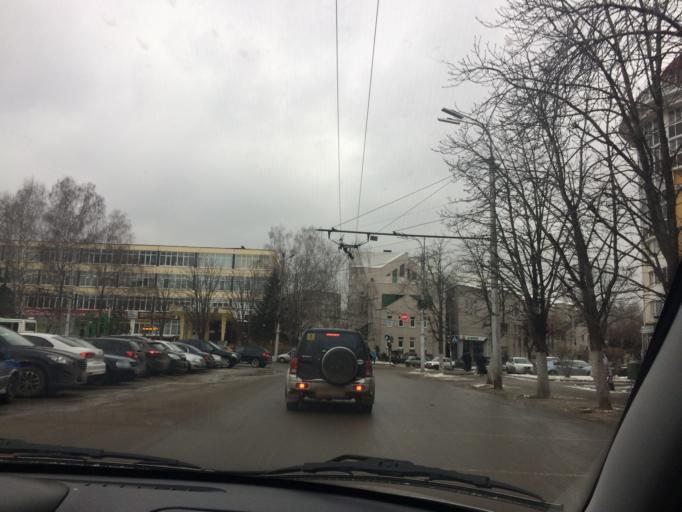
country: RU
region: Rjazan
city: Ryazan'
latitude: 54.6203
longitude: 39.7450
